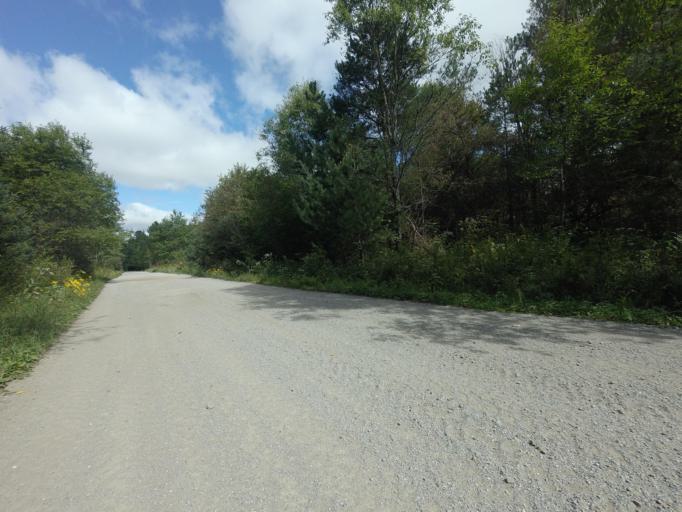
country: CA
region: Ontario
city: Omemee
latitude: 44.7490
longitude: -78.6673
